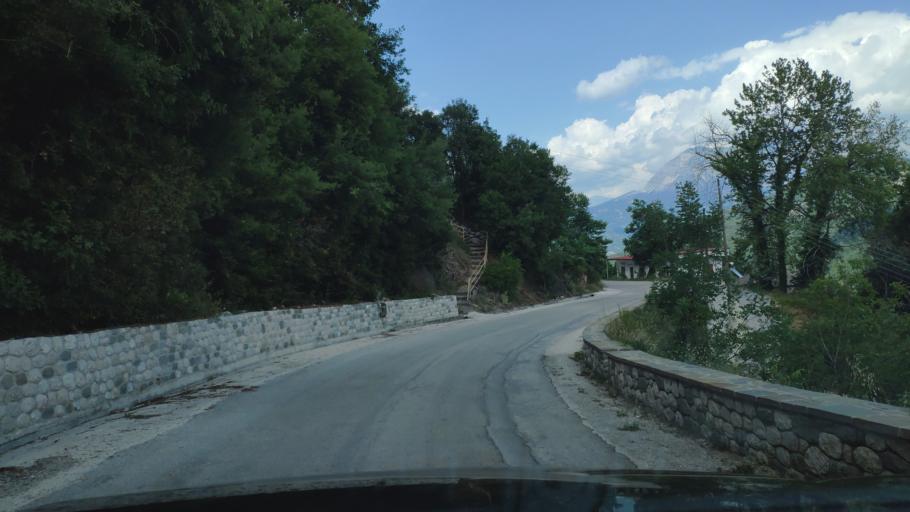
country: GR
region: Epirus
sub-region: Nomos Artas
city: Agios Dimitrios
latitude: 39.4189
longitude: 21.0111
